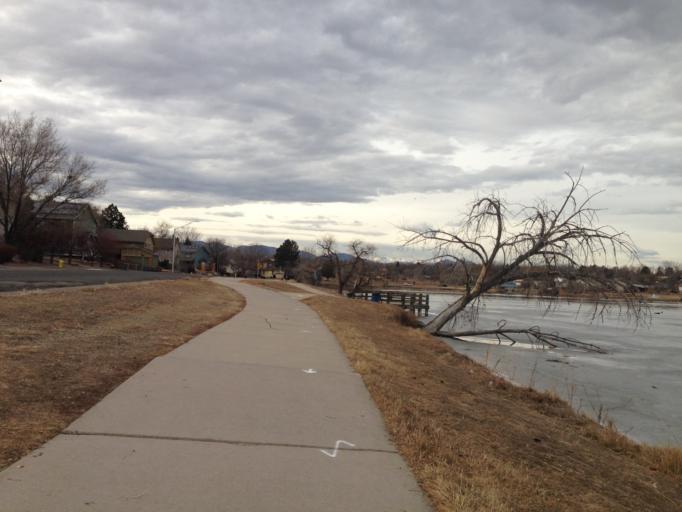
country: US
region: Colorado
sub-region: Adams County
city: Westminster
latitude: 39.8424
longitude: -105.0679
